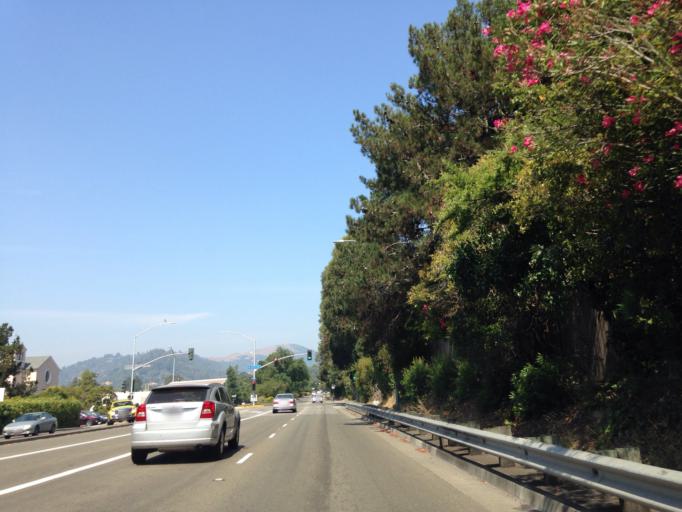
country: US
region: California
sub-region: Marin County
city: Larkspur
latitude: 37.9503
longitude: -122.5328
